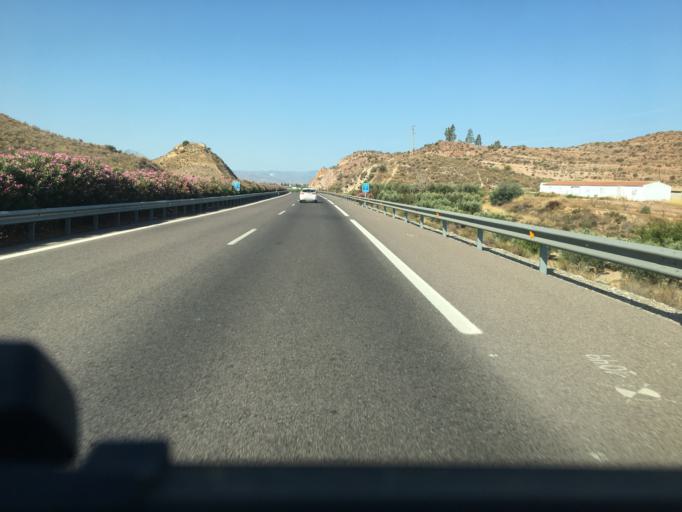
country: ES
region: Andalusia
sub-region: Provincia de Almeria
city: Huercal-Overa
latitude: 37.4195
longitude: -1.9396
